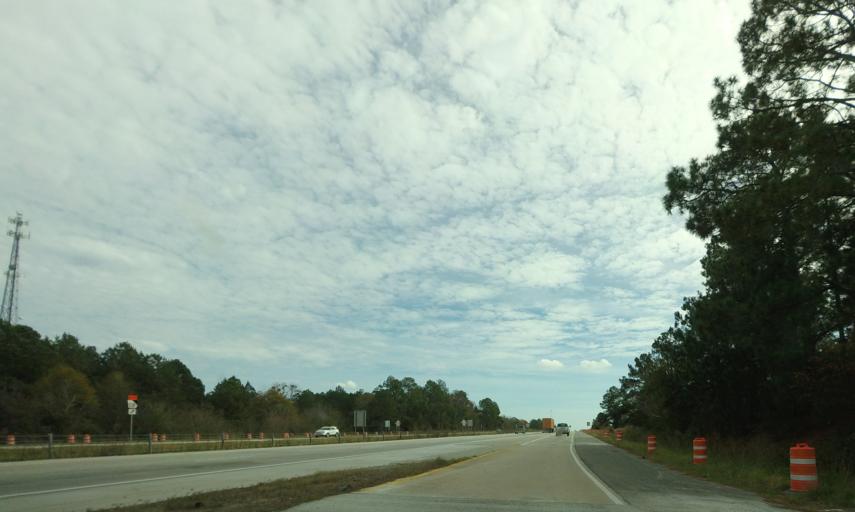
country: US
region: Georgia
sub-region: Dodge County
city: Chester
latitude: 32.5201
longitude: -83.0870
